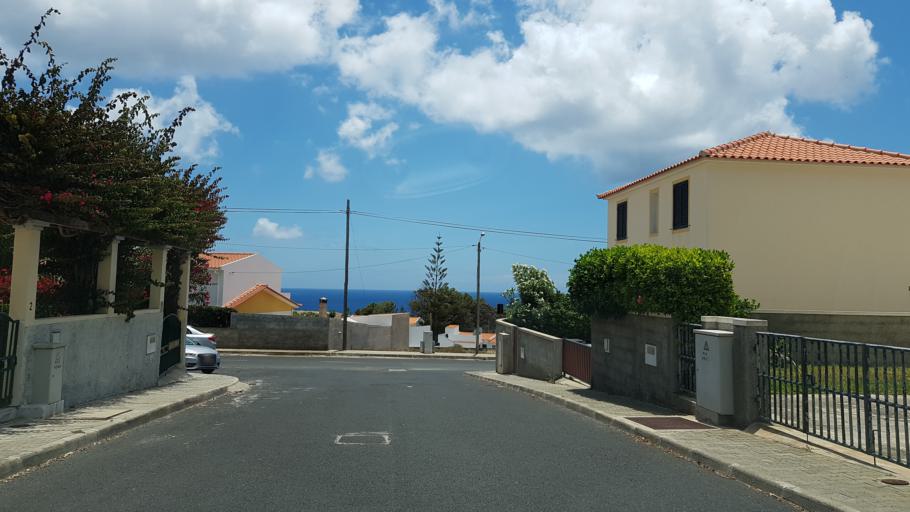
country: PT
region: Madeira
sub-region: Porto Santo
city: Vila de Porto Santo
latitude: 33.0614
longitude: -16.3537
